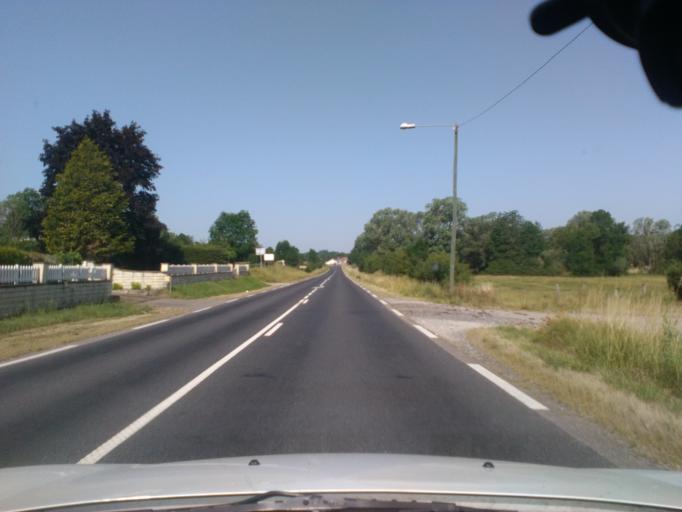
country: FR
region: Lorraine
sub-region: Departement des Vosges
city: Mirecourt
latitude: 48.3074
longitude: 6.1137
